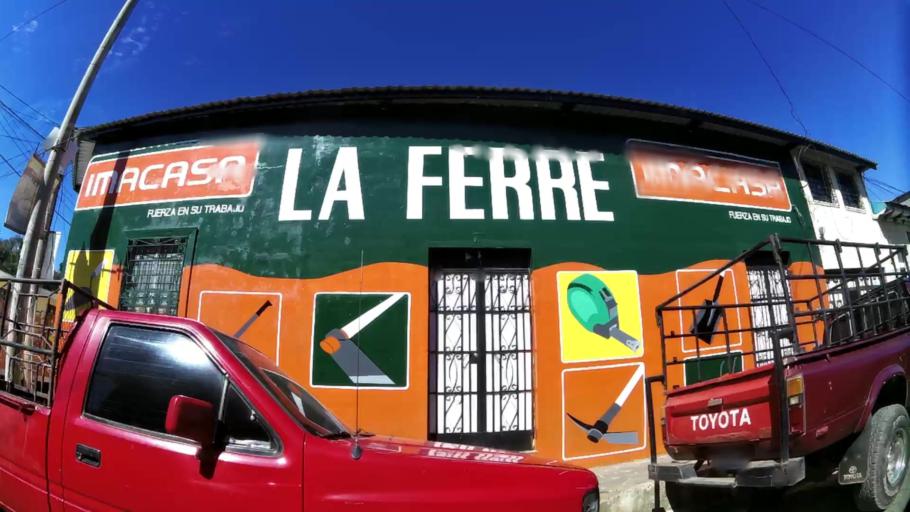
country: SV
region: Ahuachapan
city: Concepcion de Ataco
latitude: 13.8681
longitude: -89.8510
